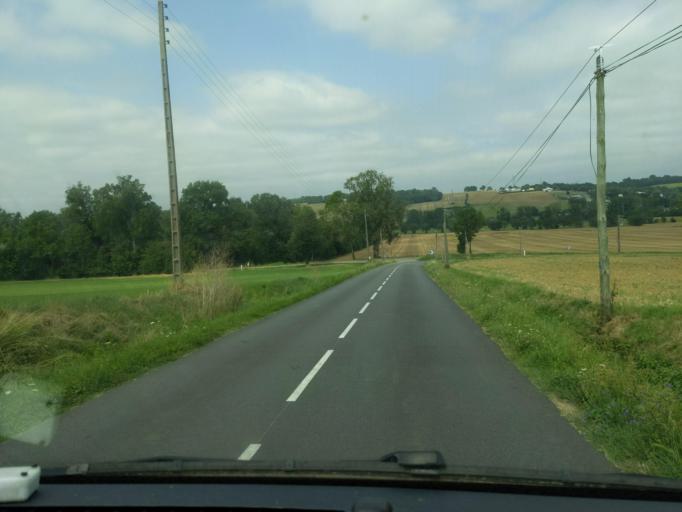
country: FR
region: Midi-Pyrenees
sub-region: Departement de la Haute-Garonne
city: Saint-Orens-de-Gameville
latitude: 43.5697
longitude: 1.5403
